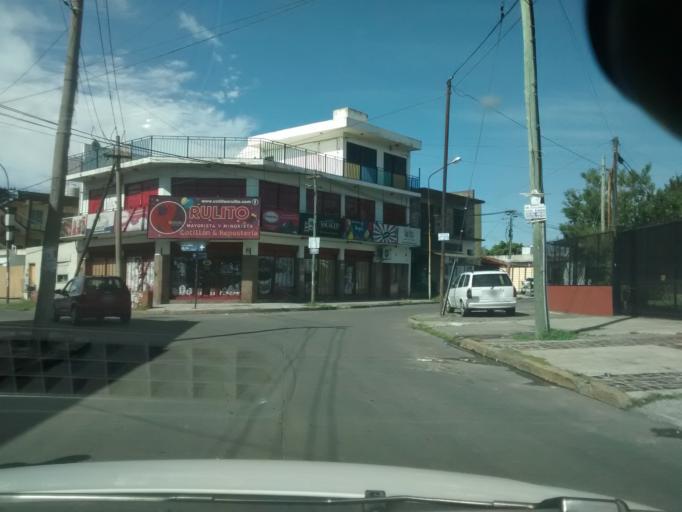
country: AR
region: Buenos Aires
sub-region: Partido de Moron
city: Moron
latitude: -34.6608
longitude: -58.6229
